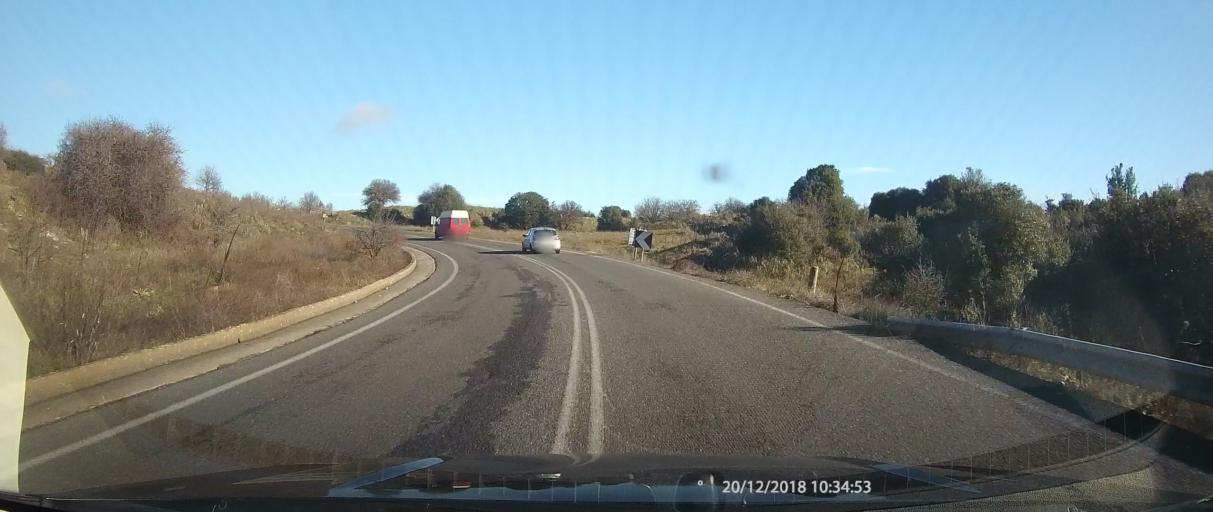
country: GR
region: Peloponnese
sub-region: Nomos Lakonias
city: Kariai
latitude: 37.3526
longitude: 22.4133
